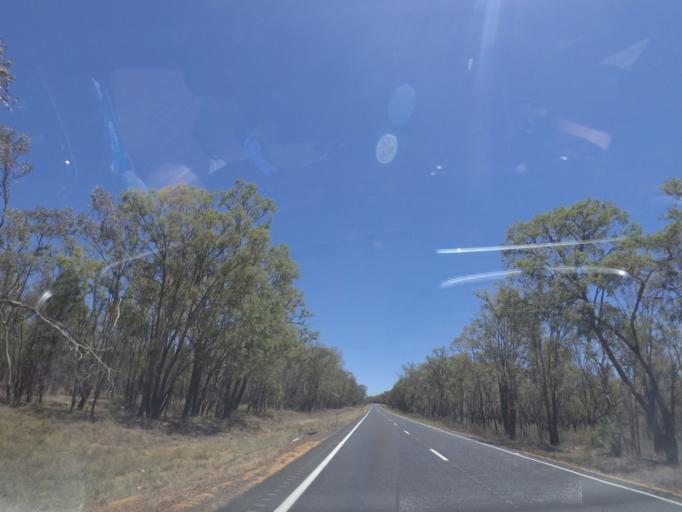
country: AU
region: New South Wales
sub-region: Warrumbungle Shire
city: Coonabarabran
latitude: -31.2012
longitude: 149.3424
